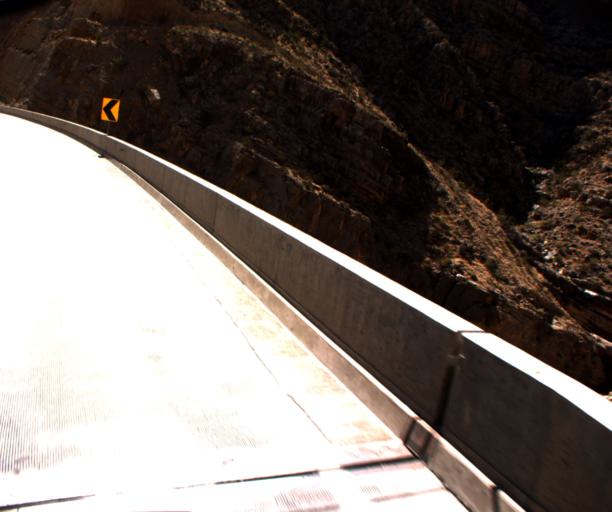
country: US
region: Arizona
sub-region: Mohave County
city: Beaver Dam
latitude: 36.9270
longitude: -113.8321
